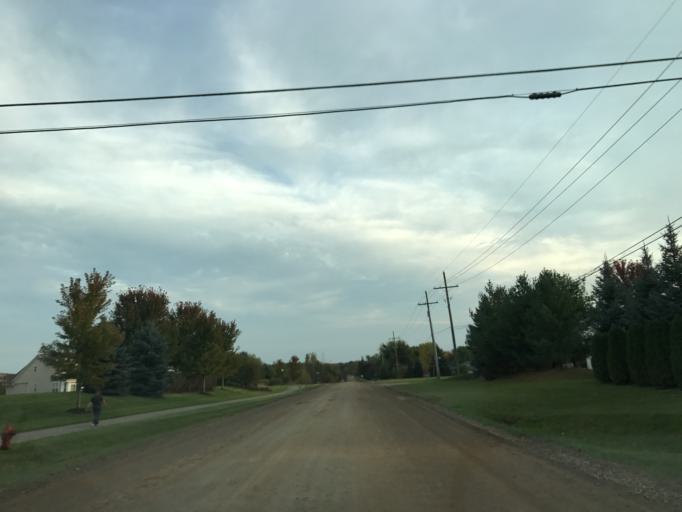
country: US
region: Michigan
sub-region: Oakland County
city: South Lyon
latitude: 42.4838
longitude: -83.6187
